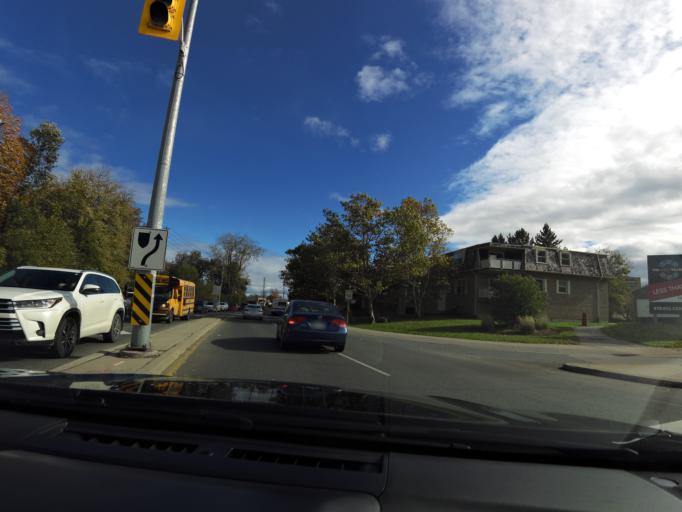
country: CA
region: Ontario
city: Waterloo
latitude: 43.4642
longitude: -80.5414
